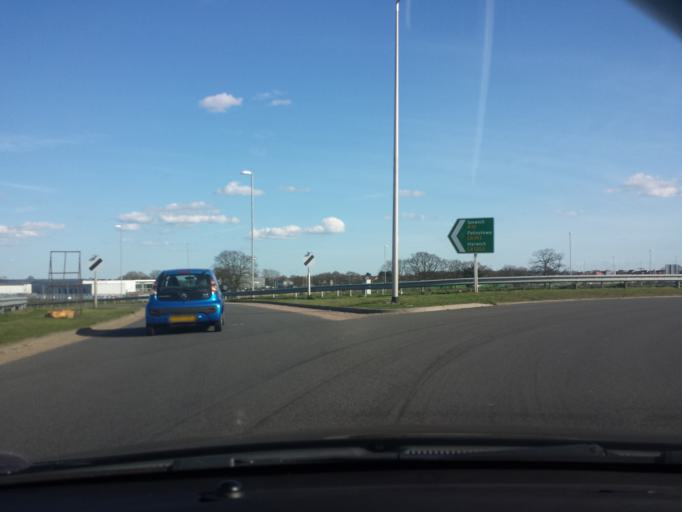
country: GB
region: England
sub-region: Essex
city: Great Horkesley
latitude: 51.9255
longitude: 0.9006
